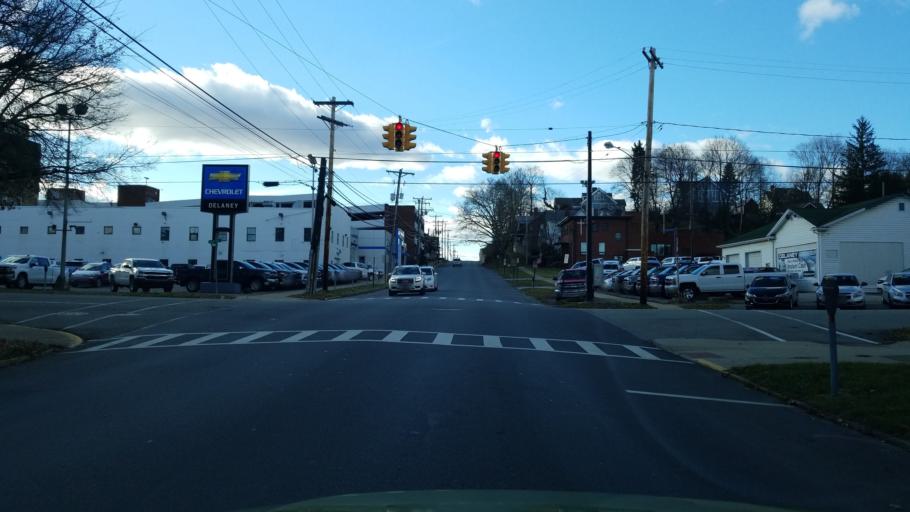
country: US
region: Pennsylvania
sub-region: Indiana County
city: Indiana
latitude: 40.6243
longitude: -79.1505
